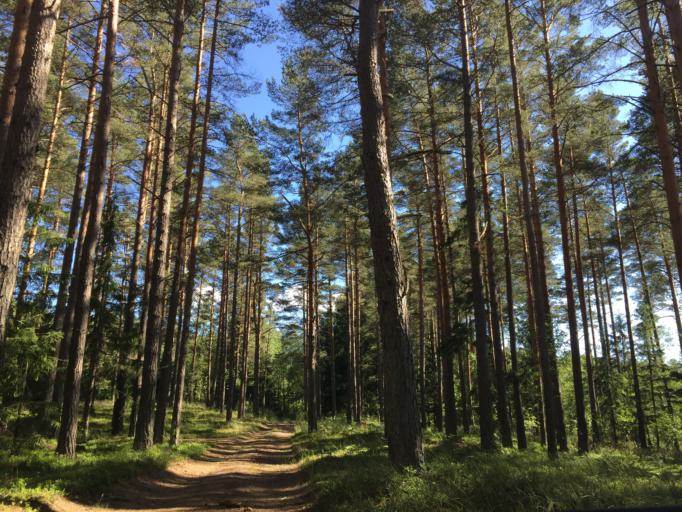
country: LV
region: Ventspils
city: Ventspils
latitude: 57.4659
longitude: 21.6527
